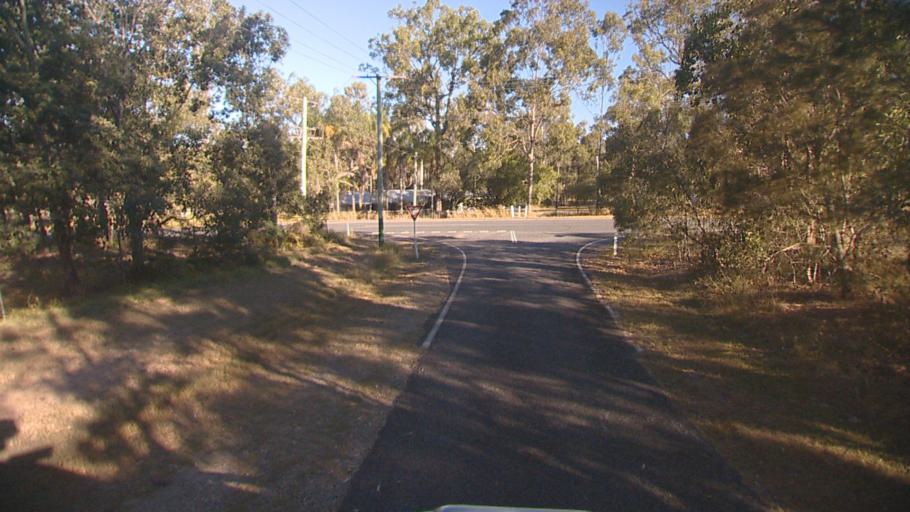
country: AU
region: Queensland
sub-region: Logan
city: North Maclean
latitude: -27.7546
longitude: 153.0053
